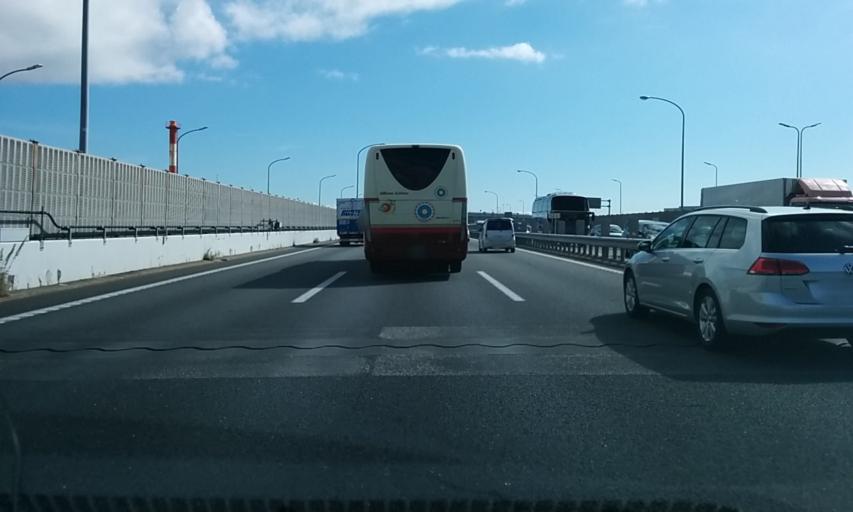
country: JP
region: Hyogo
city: Kawanishi
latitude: 34.8110
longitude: 135.4145
